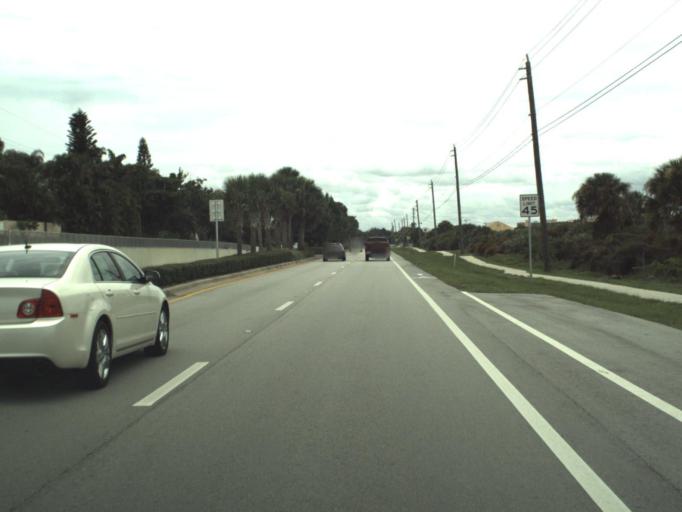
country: US
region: Florida
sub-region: Palm Beach County
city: Juno Beach
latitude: 26.8730
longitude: -80.0551
